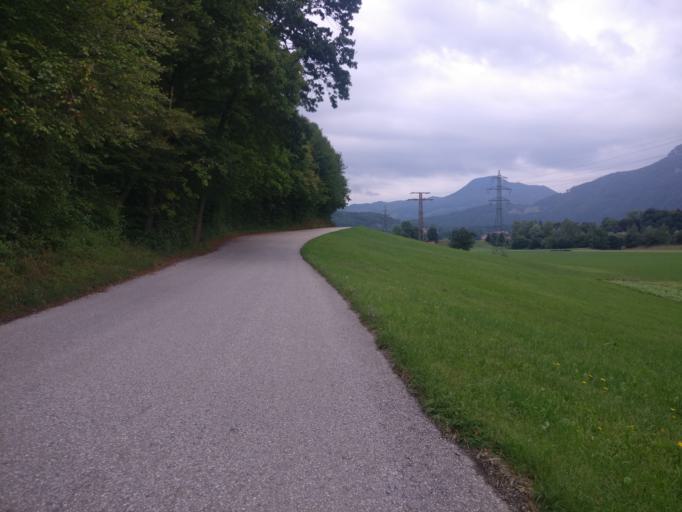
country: AT
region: Styria
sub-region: Politischer Bezirk Graz-Umgebung
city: Frohnleiten
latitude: 47.2572
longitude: 15.3123
